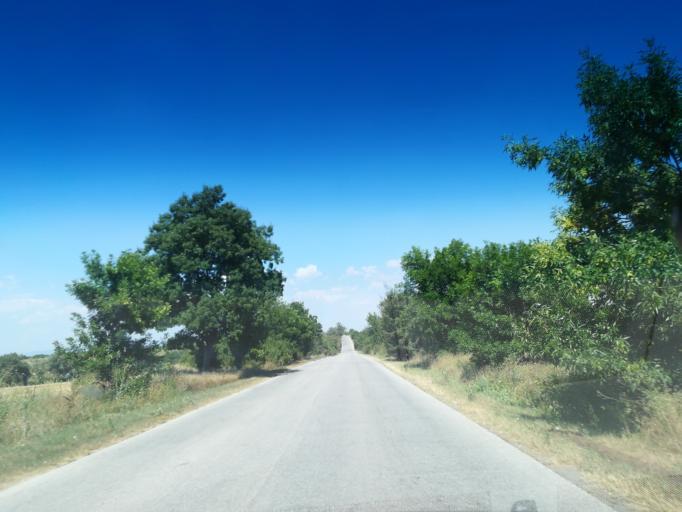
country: BG
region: Plovdiv
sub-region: Obshtina Sadovo
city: Sadovo
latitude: 42.0530
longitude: 25.1496
